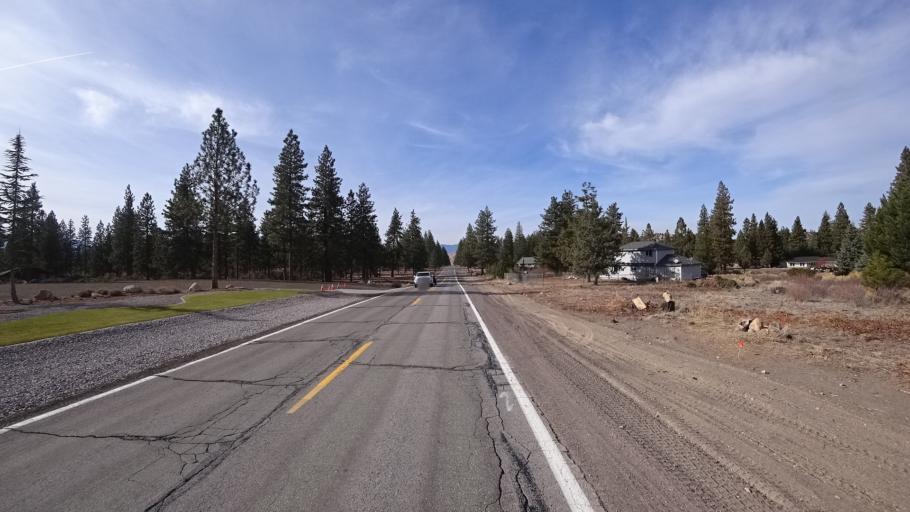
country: US
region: California
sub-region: Siskiyou County
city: Weed
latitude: 41.4940
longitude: -122.3671
